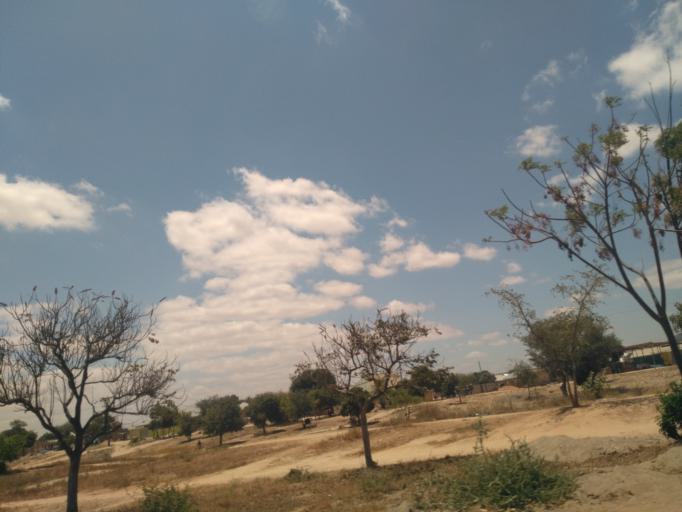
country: TZ
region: Dodoma
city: Dodoma
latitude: -6.1748
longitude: 35.7639
